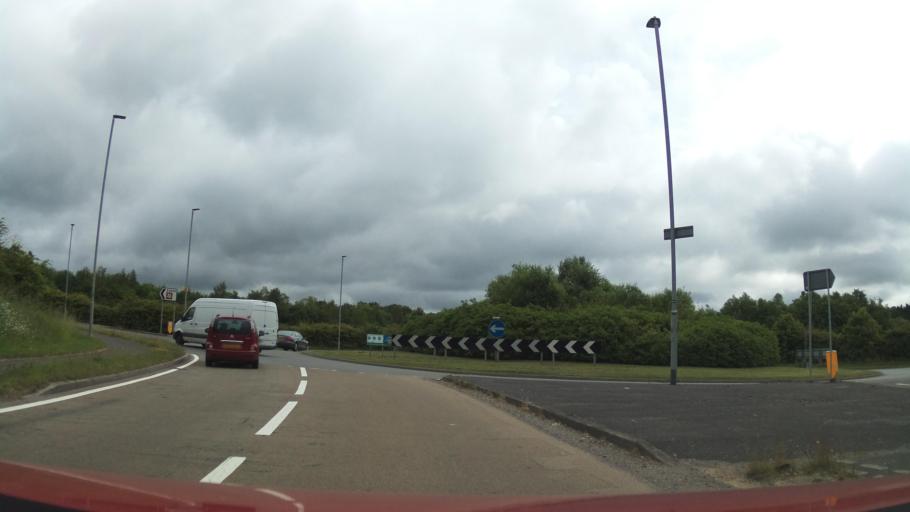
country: GB
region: England
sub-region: Leicestershire
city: Ashby de la Zouch
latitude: 52.7621
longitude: -1.4787
